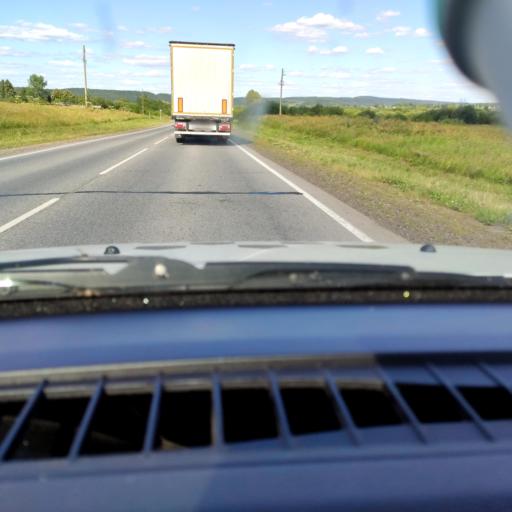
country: RU
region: Perm
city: Ocher
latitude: 57.4947
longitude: 54.5069
